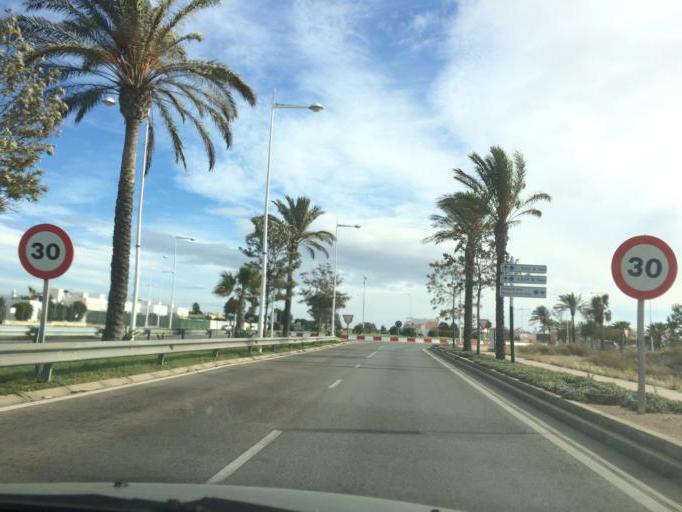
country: ES
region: Andalusia
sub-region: Provincia de Almeria
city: Retamar
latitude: 36.8520
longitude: -2.3142
